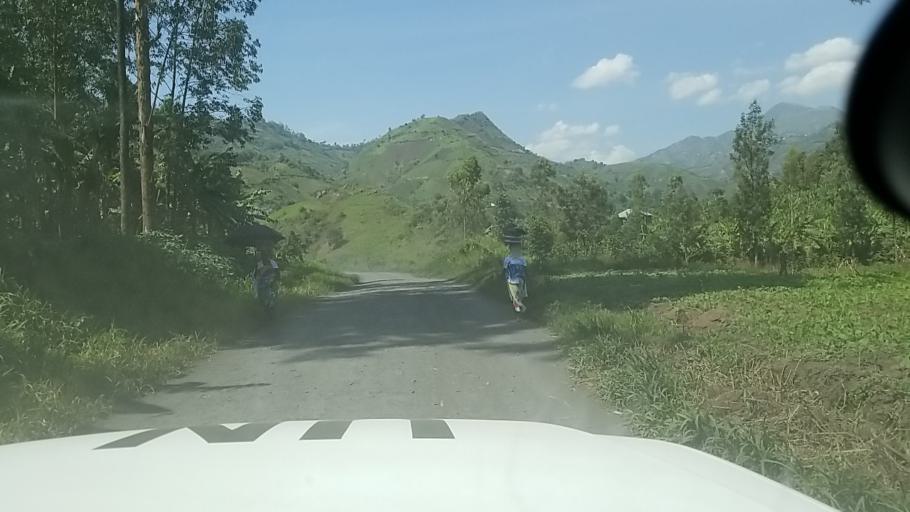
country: CD
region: Nord Kivu
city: Sake
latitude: -1.7326
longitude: 29.0072
